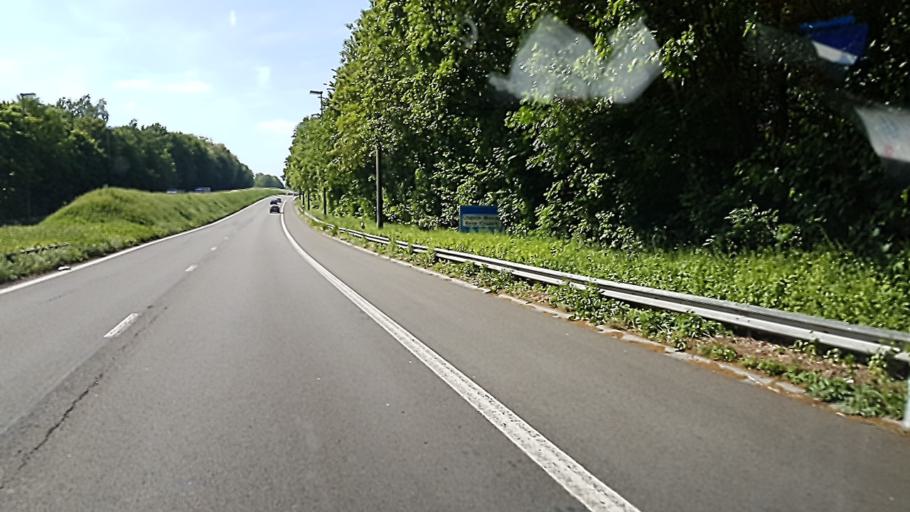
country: BE
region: Wallonia
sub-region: Province du Brabant Wallon
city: Waterloo
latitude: 50.7136
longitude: 4.4128
